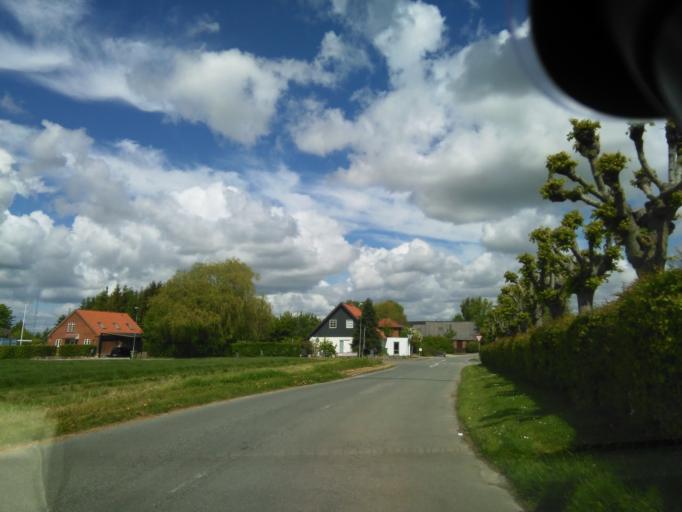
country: DK
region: Central Jutland
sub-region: Arhus Kommune
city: Solbjerg
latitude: 56.0334
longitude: 10.1032
